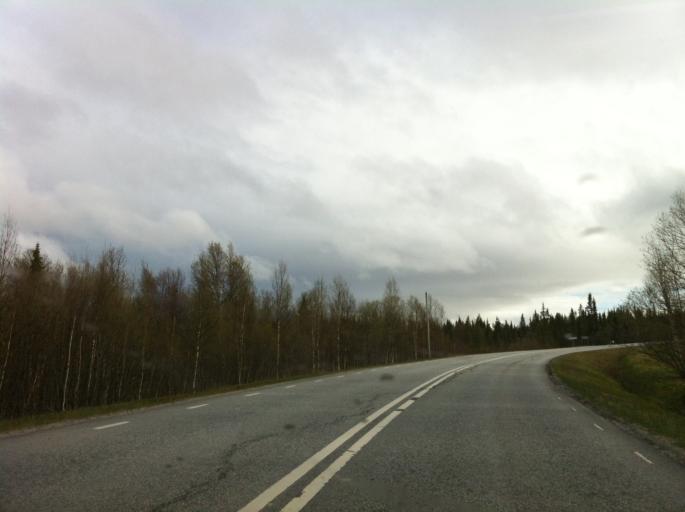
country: NO
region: Hedmark
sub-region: Engerdal
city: Engerdal
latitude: 62.5427
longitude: 12.5478
